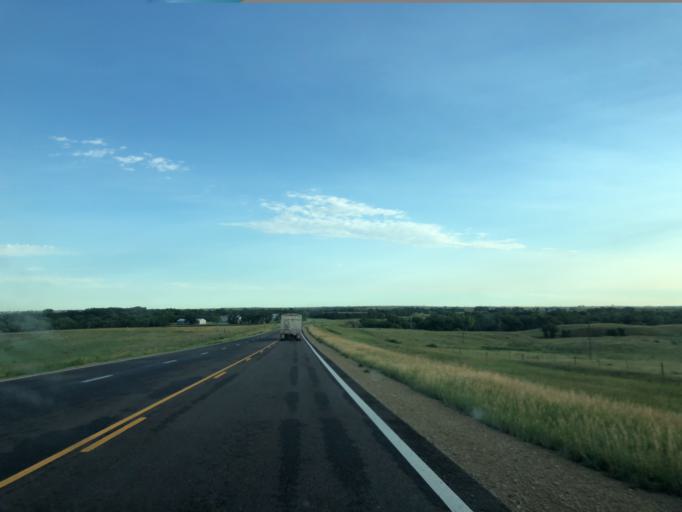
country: US
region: Kansas
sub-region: Russell County
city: Russell
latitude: 38.7629
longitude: -98.8530
